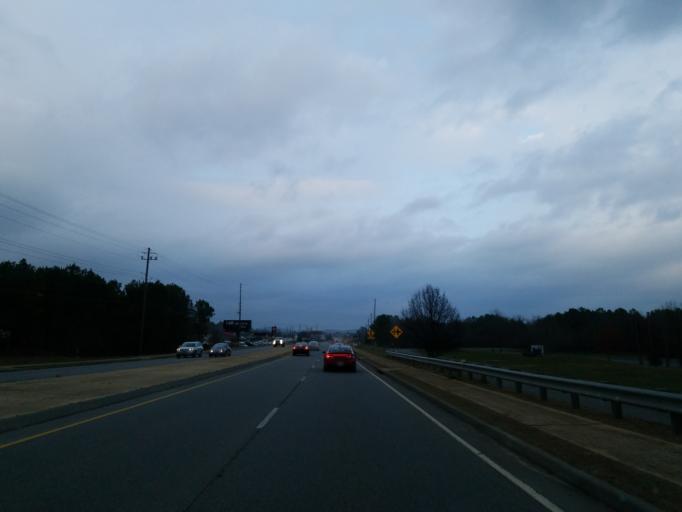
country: US
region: Georgia
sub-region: Bartow County
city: Cartersville
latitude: 34.1450
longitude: -84.8354
